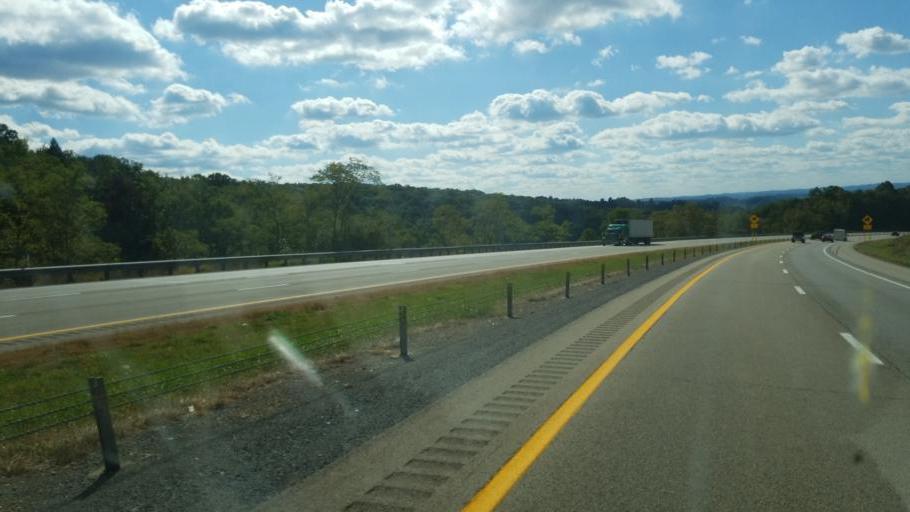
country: US
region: West Virginia
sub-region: Monongalia County
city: Cheat Lake
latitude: 39.6575
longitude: -79.8285
